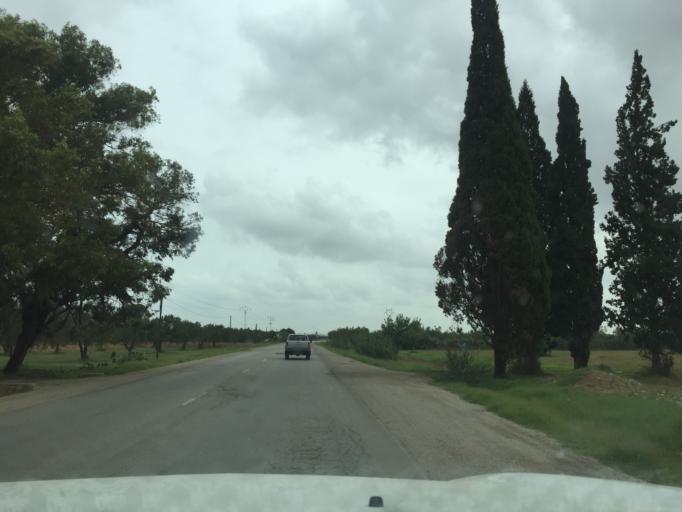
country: TN
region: Al Munastir
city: Manzil Kamil
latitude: 35.6258
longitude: 10.6951
